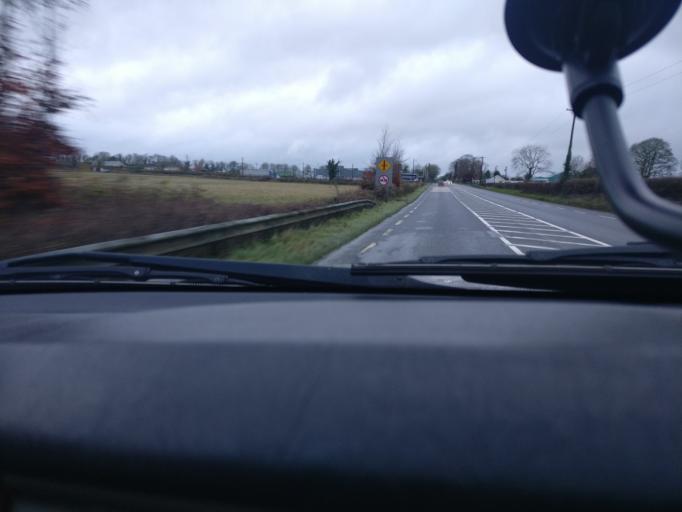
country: IE
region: Leinster
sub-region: Kildare
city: Kilcock
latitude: 53.4193
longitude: -6.7334
